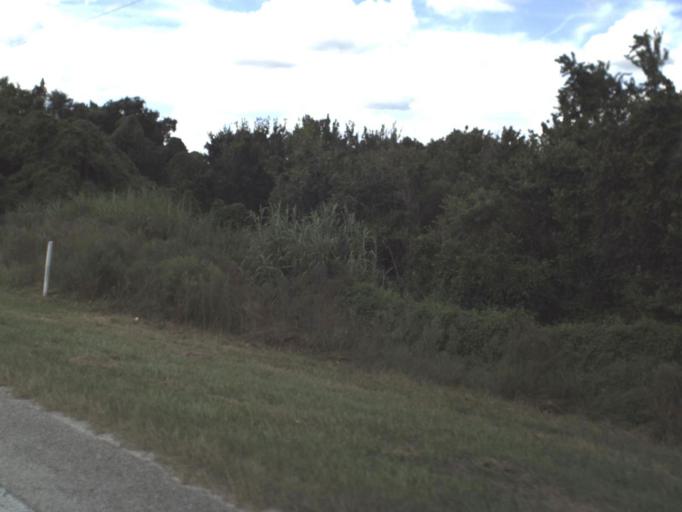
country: US
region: Florida
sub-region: Polk County
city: Fuller Heights
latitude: 27.9030
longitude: -82.0062
